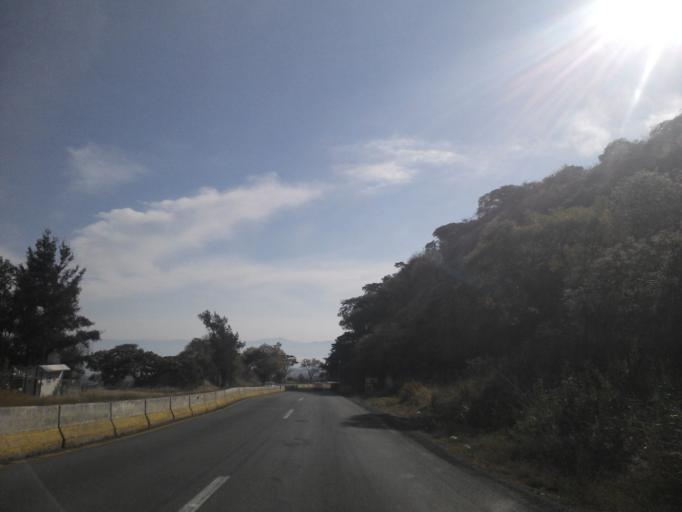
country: MX
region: Jalisco
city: Ixtlahuacan de los Membrillos
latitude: 20.3304
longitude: -103.1836
